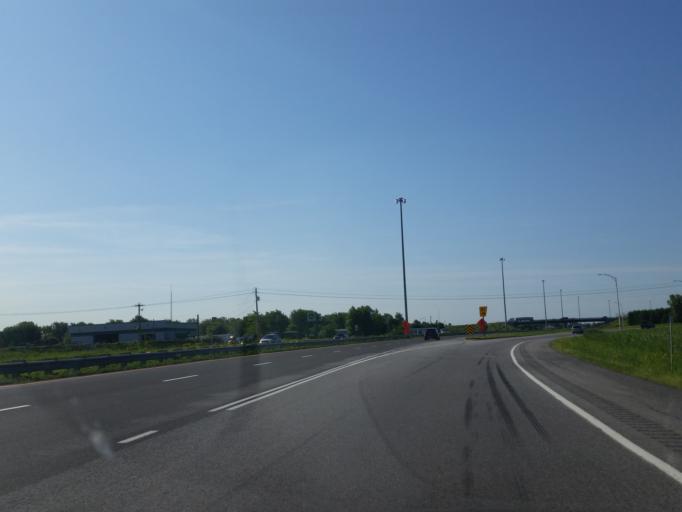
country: CA
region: Quebec
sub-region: Monteregie
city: Napierville
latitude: 45.1981
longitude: -73.4550
